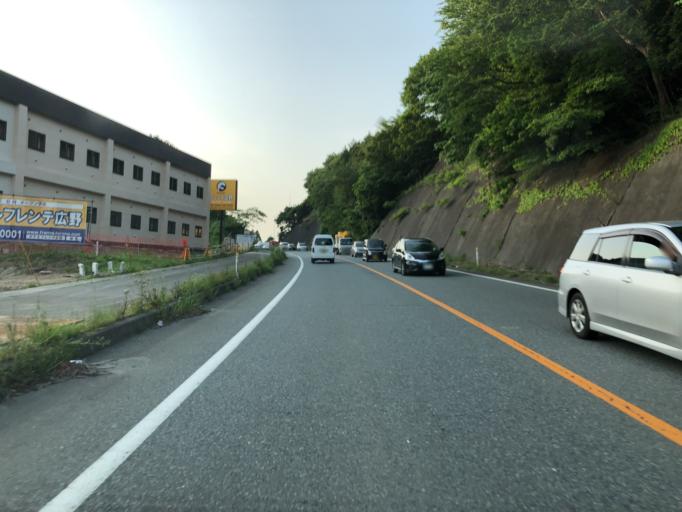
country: JP
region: Fukushima
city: Iwaki
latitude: 37.1934
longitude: 140.9995
